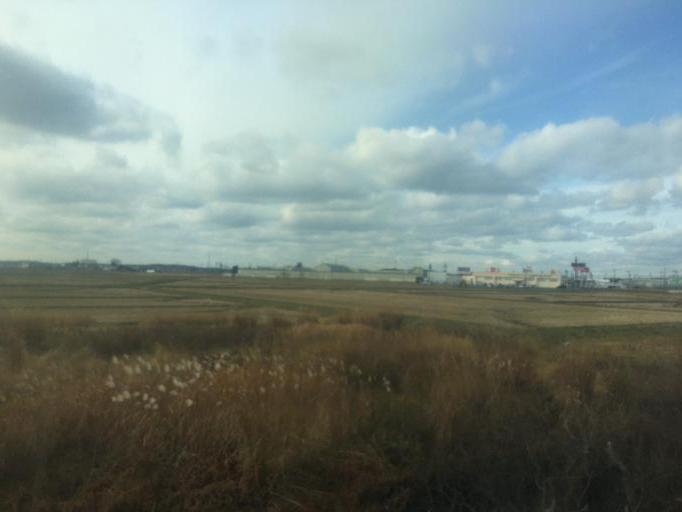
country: JP
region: Akita
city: Noshiromachi
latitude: 40.1826
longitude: 140.0590
